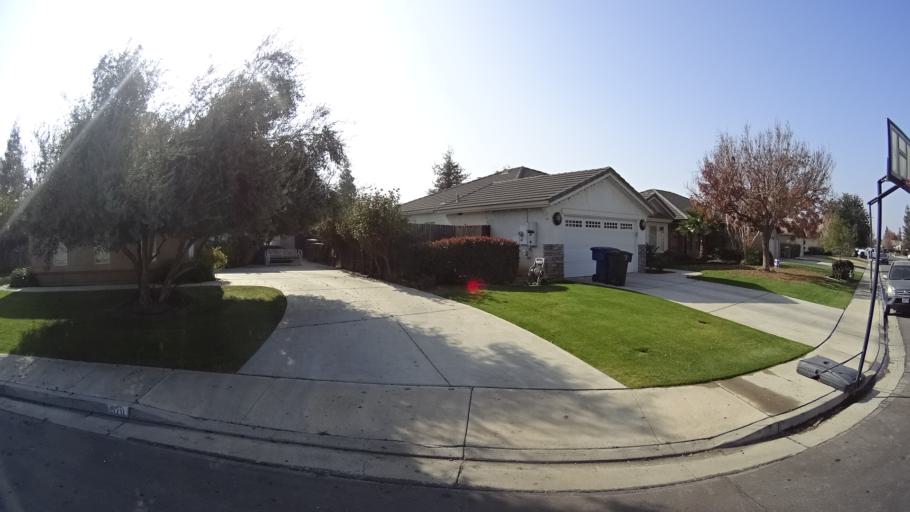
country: US
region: California
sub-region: Kern County
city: Greenacres
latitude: 35.4166
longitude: -119.1108
